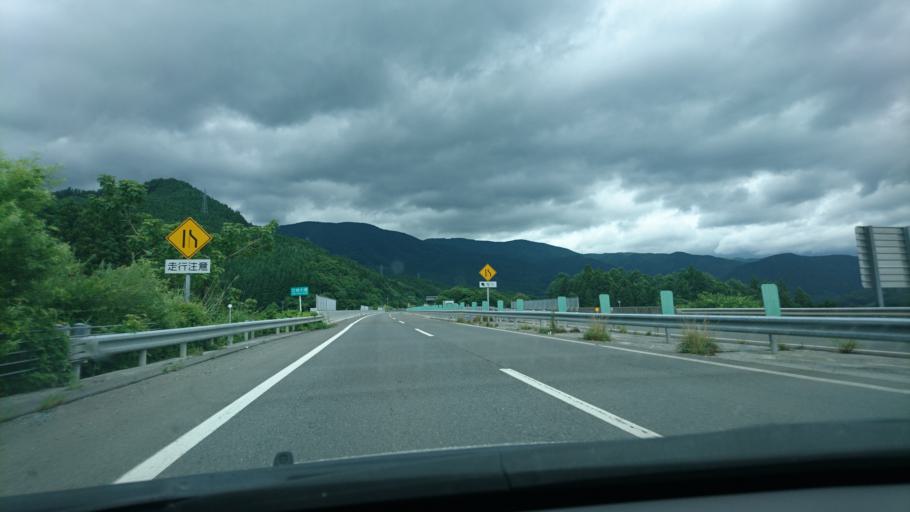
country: JP
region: Iwate
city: Ofunato
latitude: 39.1103
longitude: 141.7100
